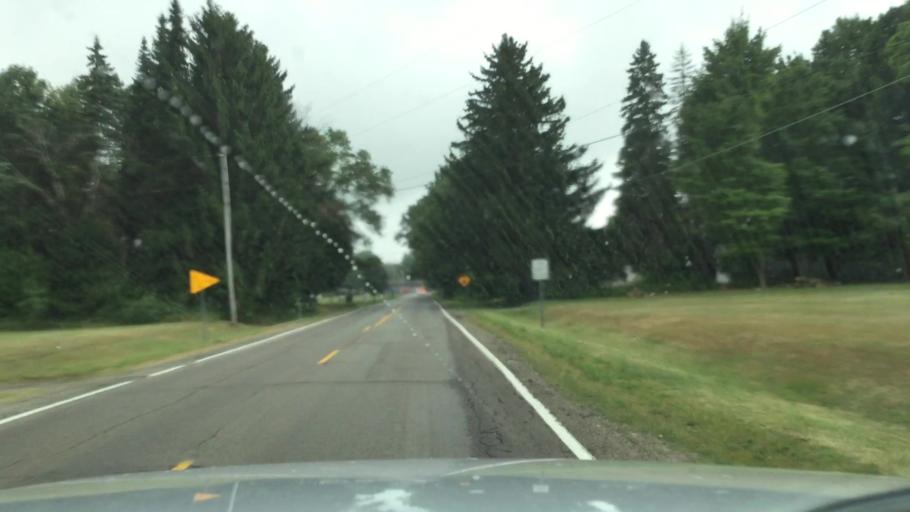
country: US
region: Michigan
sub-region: Genesee County
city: Clio
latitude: 43.1369
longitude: -83.7737
